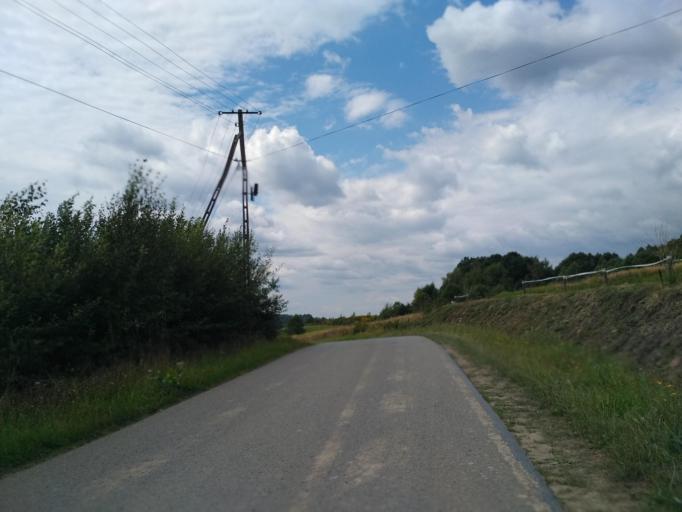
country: PL
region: Subcarpathian Voivodeship
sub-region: Powiat rzeszowski
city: Chmielnik
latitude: 49.9539
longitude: 22.1208
